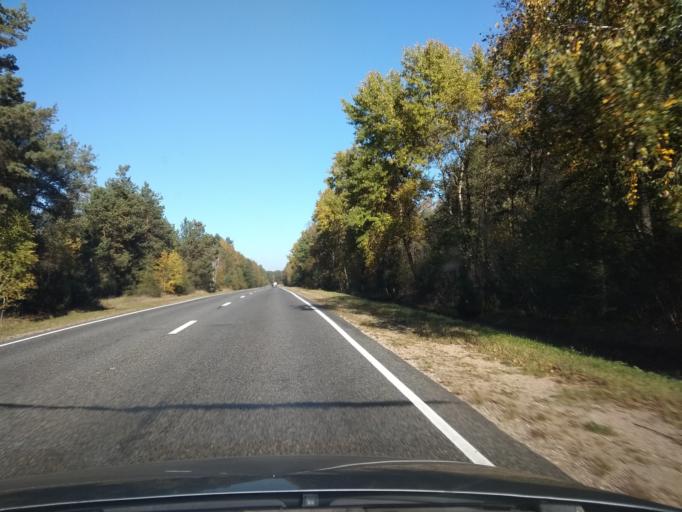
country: BY
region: Brest
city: Kobryn
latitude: 52.0912
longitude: 24.2791
